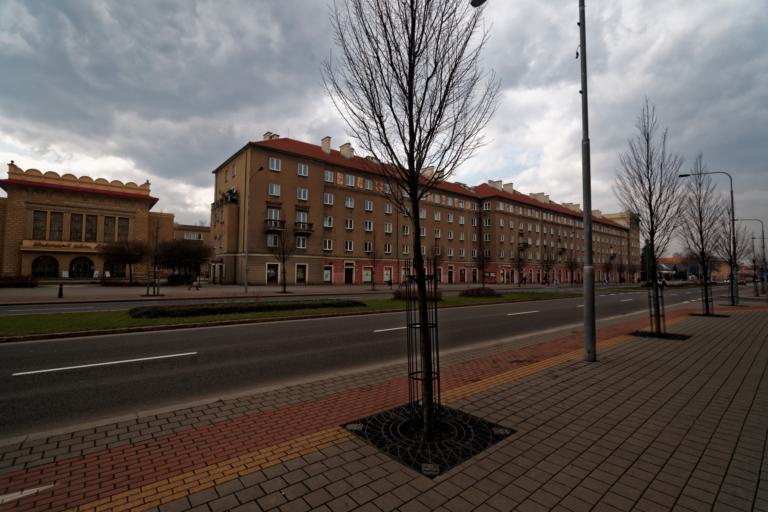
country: CZ
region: Moravskoslezsky
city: Havirov
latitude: 49.7826
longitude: 18.4266
